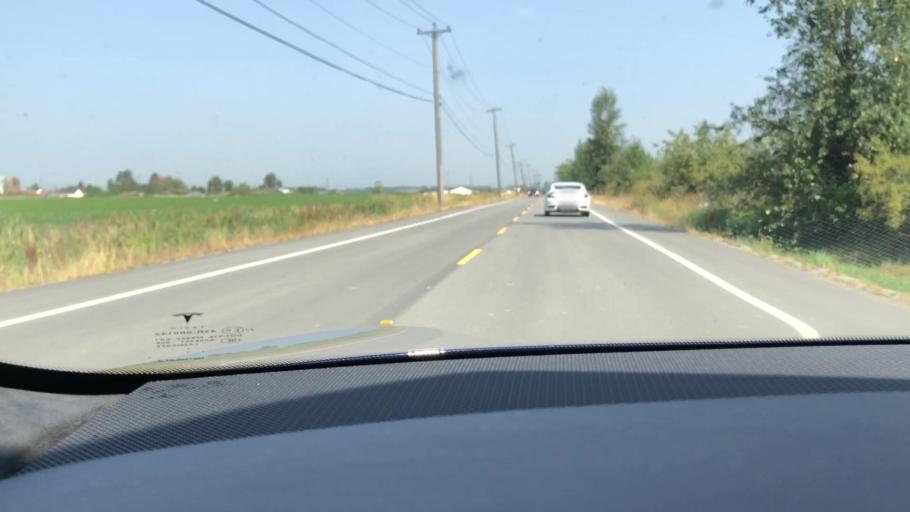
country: CA
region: British Columbia
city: Ladner
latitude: 49.0497
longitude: -123.0797
